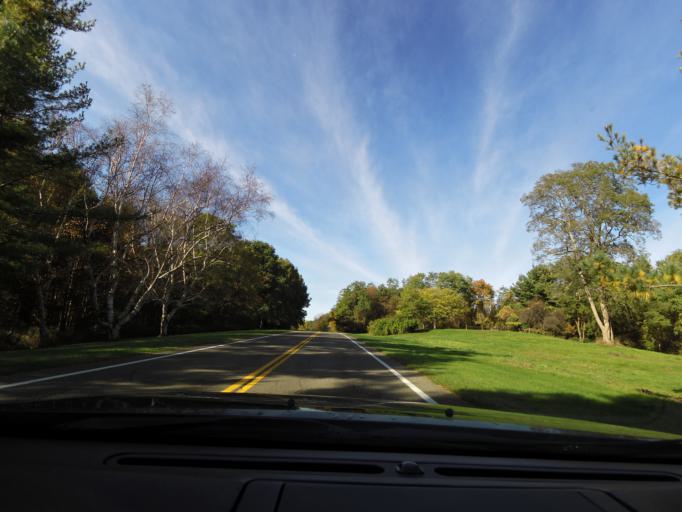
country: US
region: New York
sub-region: Livingston County
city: Mount Morris
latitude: 42.7384
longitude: -77.8960
